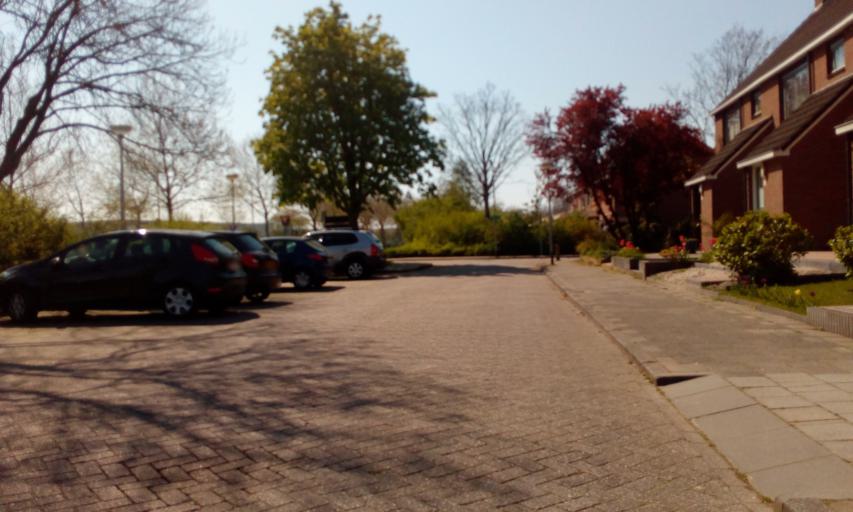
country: NL
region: South Holland
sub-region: Bodegraven-Reeuwijk
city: Bodegraven
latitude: 52.0740
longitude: 4.7584
